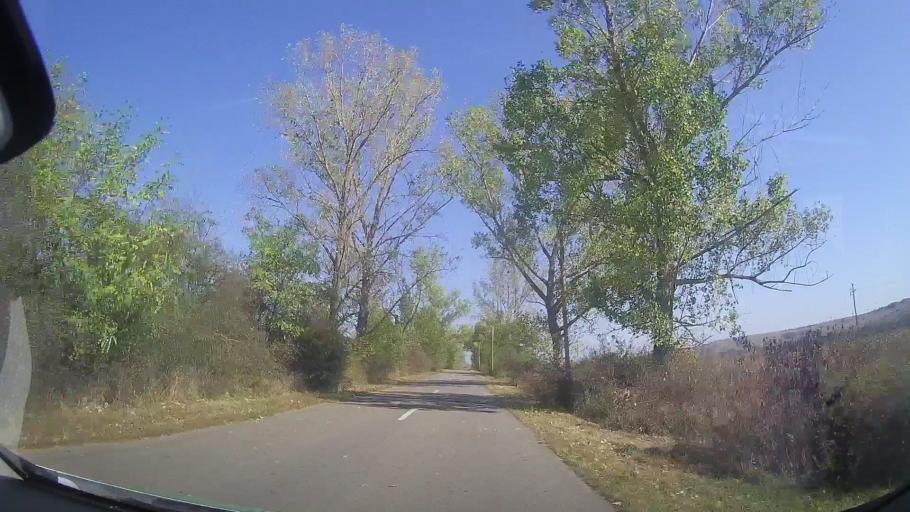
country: RO
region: Timis
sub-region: Comuna Secas
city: Secas
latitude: 45.8590
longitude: 21.8035
